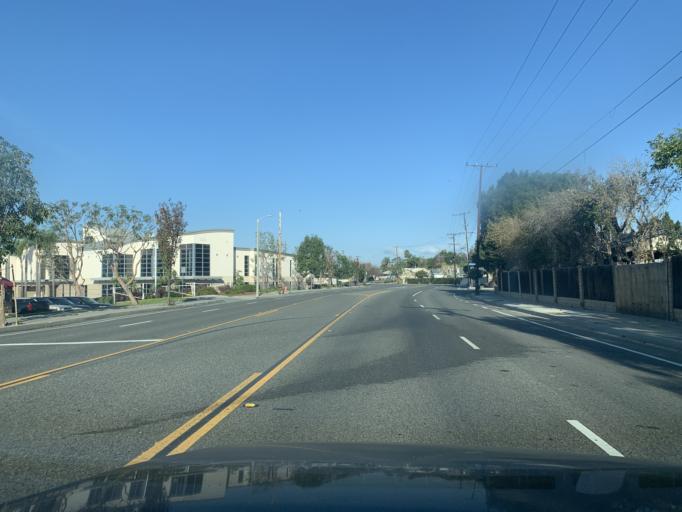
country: US
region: California
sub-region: Orange County
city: Villa Park
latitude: 33.8246
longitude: -117.8269
